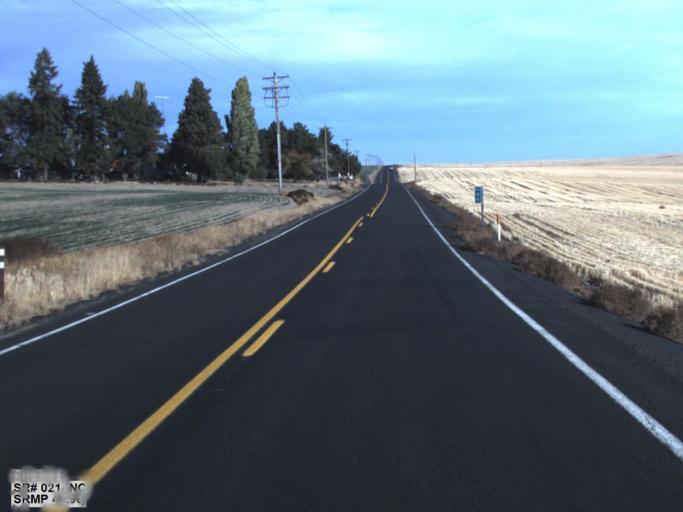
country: US
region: Washington
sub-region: Adams County
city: Ritzville
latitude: 47.2413
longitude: -118.6861
